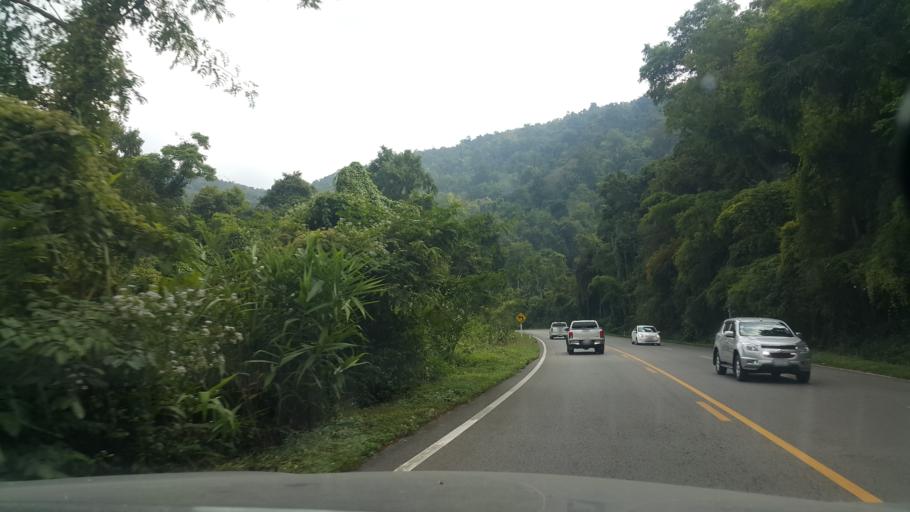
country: TH
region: Phayao
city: Phayao
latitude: 19.0666
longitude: 99.8043
